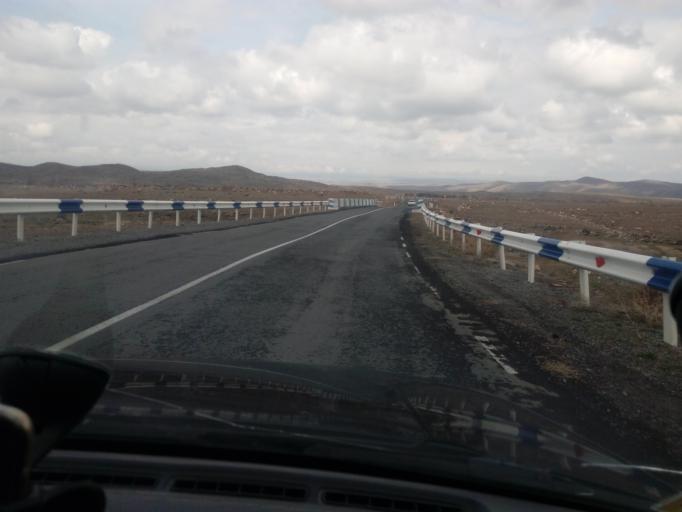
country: AM
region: Aragatsotn
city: Arteni
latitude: 40.2858
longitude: 43.7958
